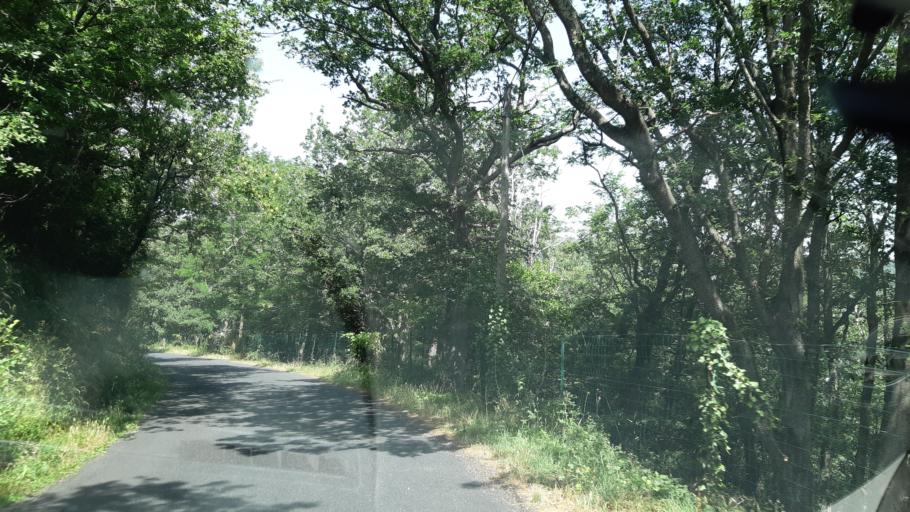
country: FR
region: Languedoc-Roussillon
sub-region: Departement des Pyrenees-Orientales
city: els Banys d'Arles
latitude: 42.5256
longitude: 2.6300
